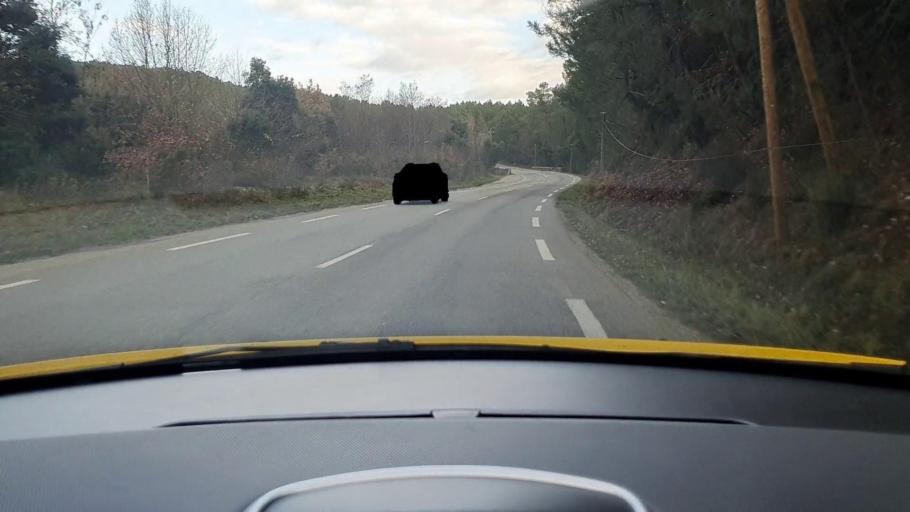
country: FR
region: Languedoc-Roussillon
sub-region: Departement du Gard
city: Les Salles-du-Gardon
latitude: 44.2567
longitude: 4.0457
